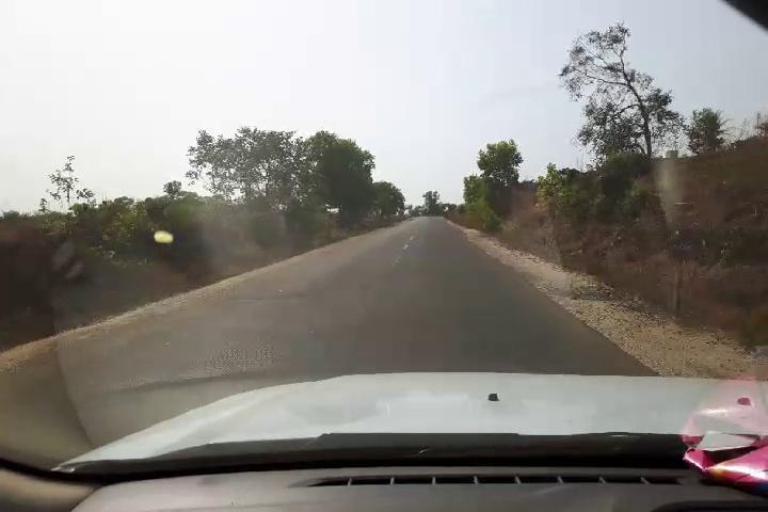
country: SL
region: Western Area
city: Hastings
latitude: 8.3142
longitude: -13.1885
